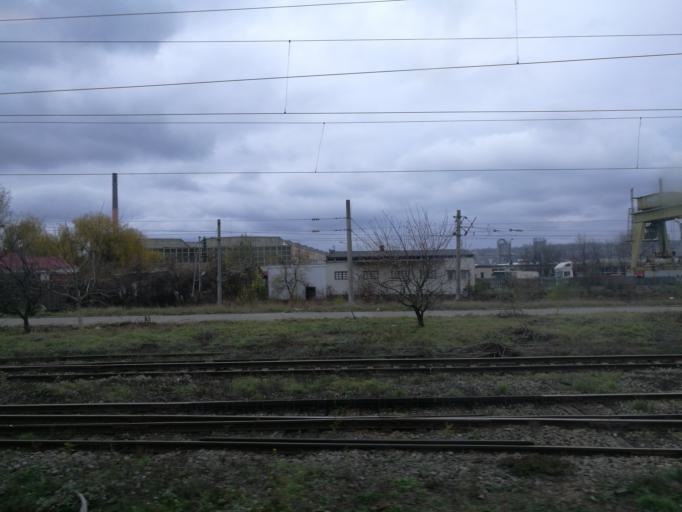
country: RO
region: Suceava
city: Suceava
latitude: 47.6684
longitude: 26.2708
